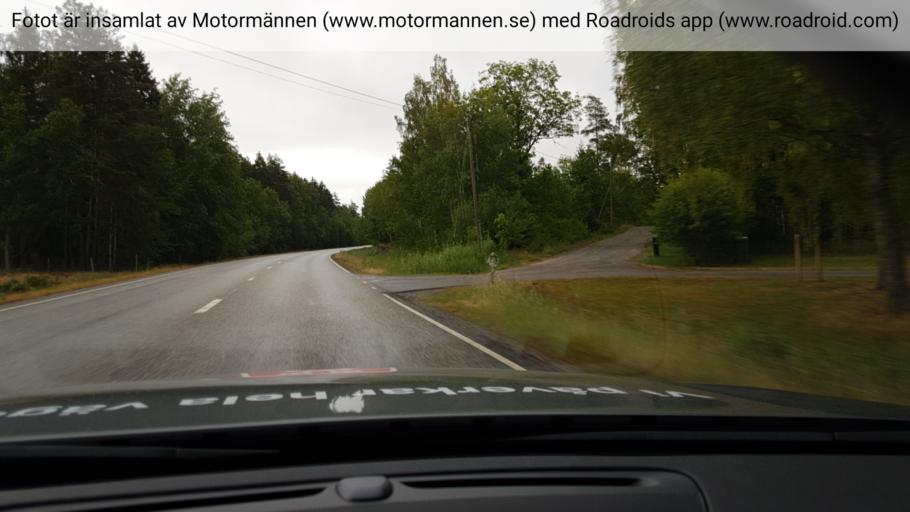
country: SE
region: Vaestmanland
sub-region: Kungsors Kommun
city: Kungsoer
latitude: 59.2993
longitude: 16.2149
